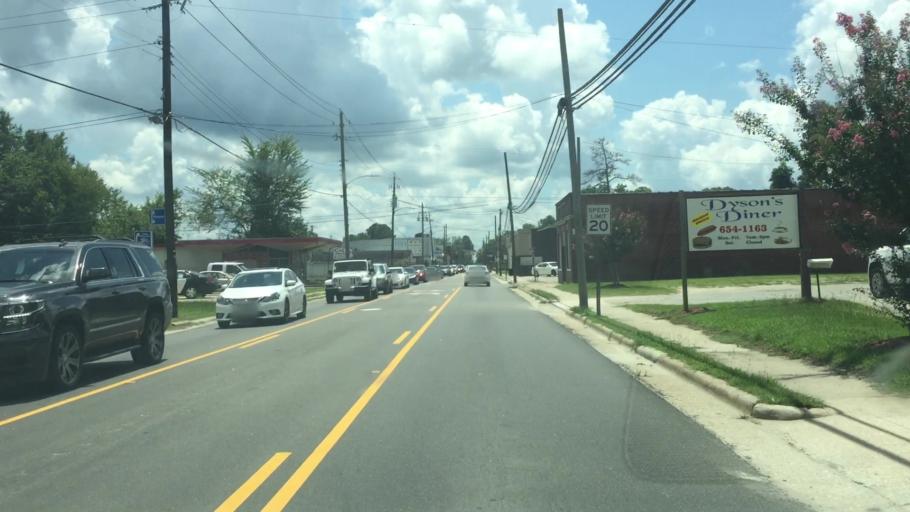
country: US
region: North Carolina
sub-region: Columbus County
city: Chadbourn
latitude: 34.3261
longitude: -78.8265
